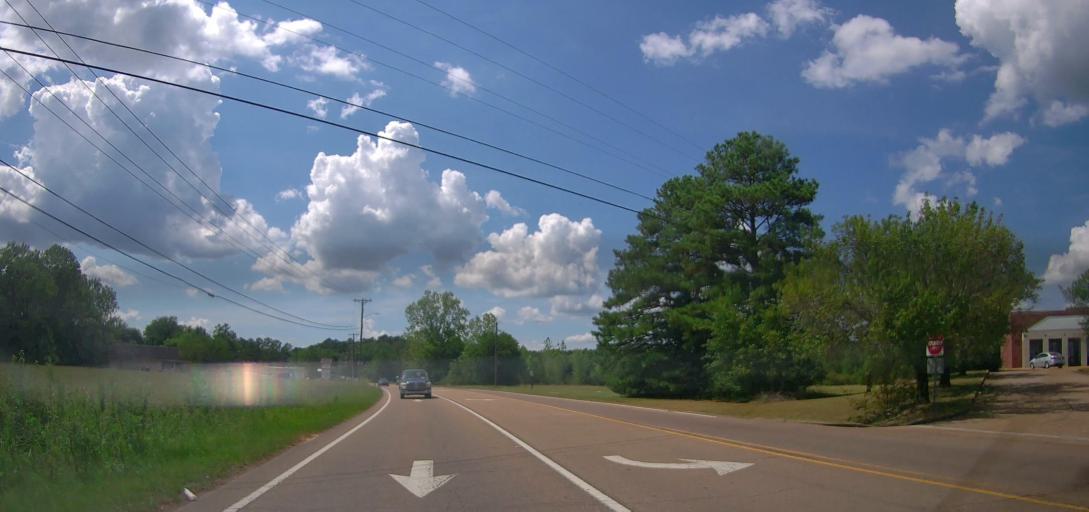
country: US
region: Mississippi
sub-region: Lowndes County
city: Columbus
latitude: 33.5352
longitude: -88.4284
